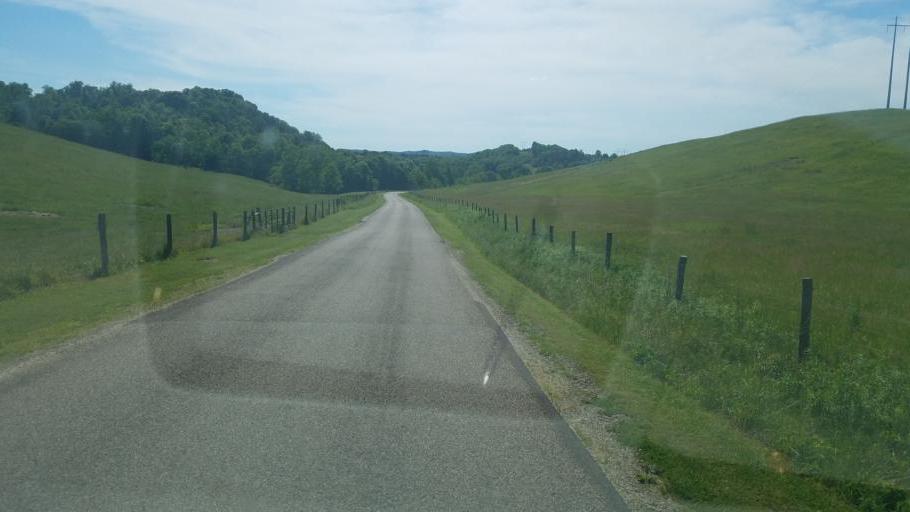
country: US
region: Ohio
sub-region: Coshocton County
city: West Lafayette
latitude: 40.2412
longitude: -81.6979
